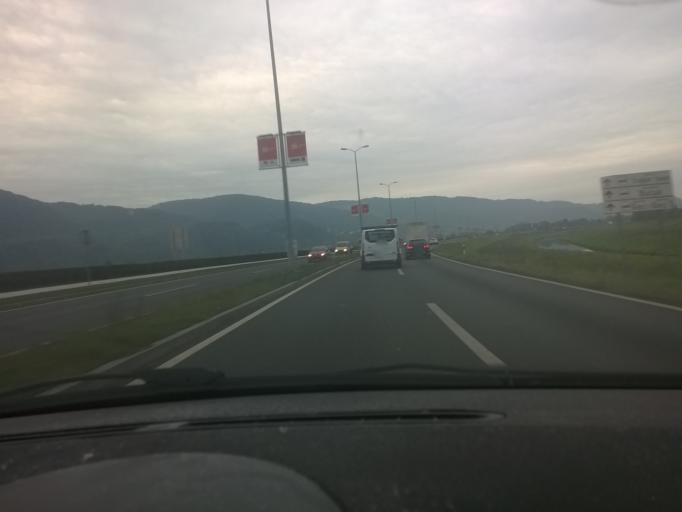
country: HR
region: Zagrebacka
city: Zapresic
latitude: 45.8669
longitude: 15.8264
